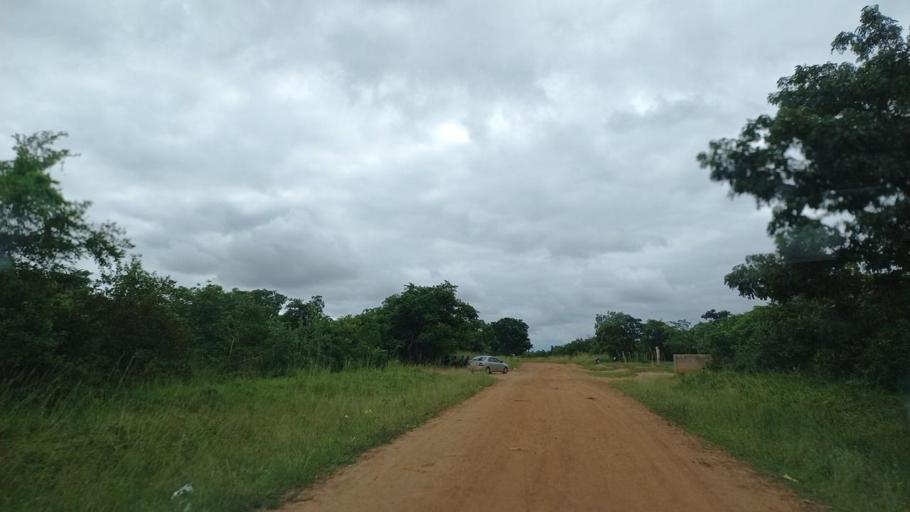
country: ZM
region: Lusaka
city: Chongwe
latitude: -15.4566
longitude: 28.8721
